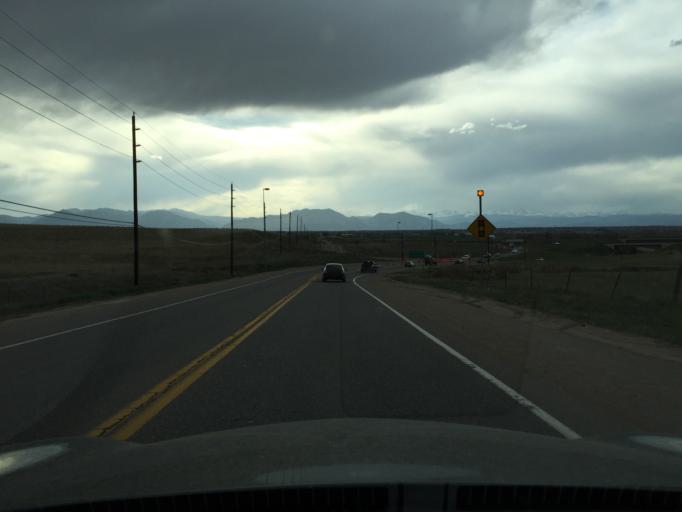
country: US
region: Colorado
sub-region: Boulder County
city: Lafayette
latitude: 39.9579
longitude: -105.0795
